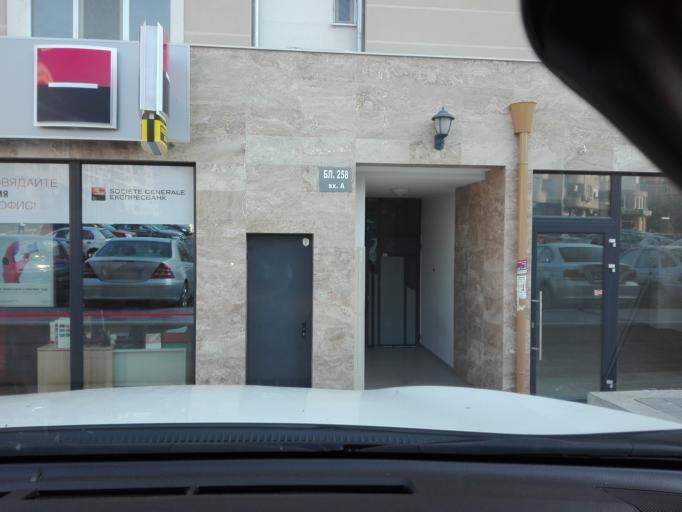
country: BG
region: Burgas
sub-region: Obshtina Burgas
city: Burgas
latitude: 42.4630
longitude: 27.4139
